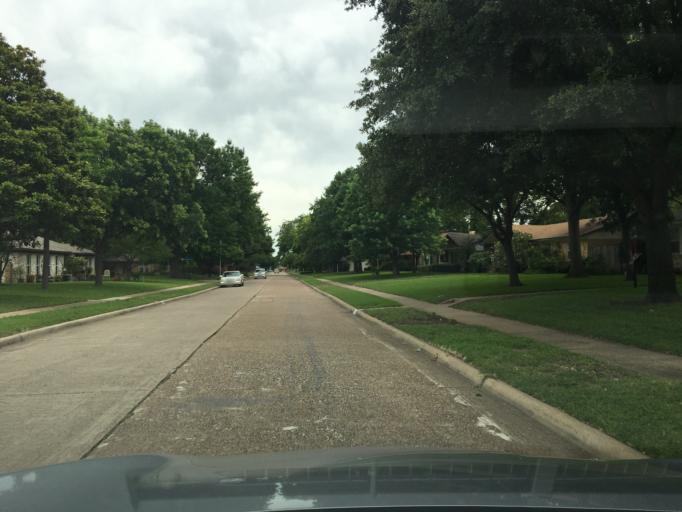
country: US
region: Texas
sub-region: Dallas County
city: Richardson
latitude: 32.9326
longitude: -96.7044
